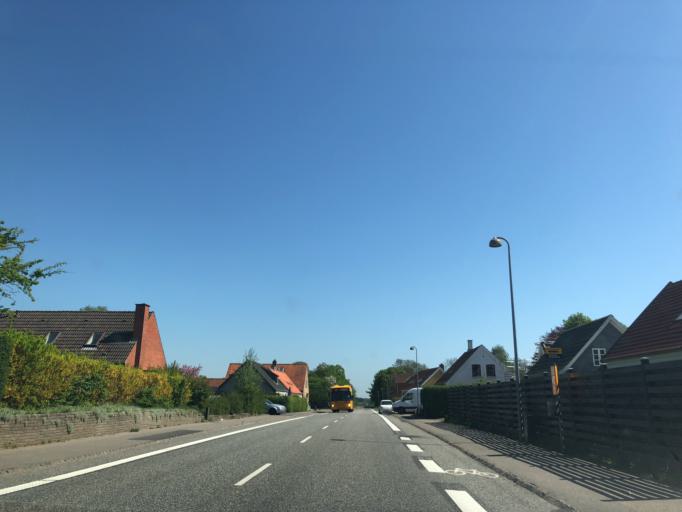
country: DK
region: Zealand
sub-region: Slagelse Kommune
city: Skaelskor
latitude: 55.3039
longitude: 11.2678
